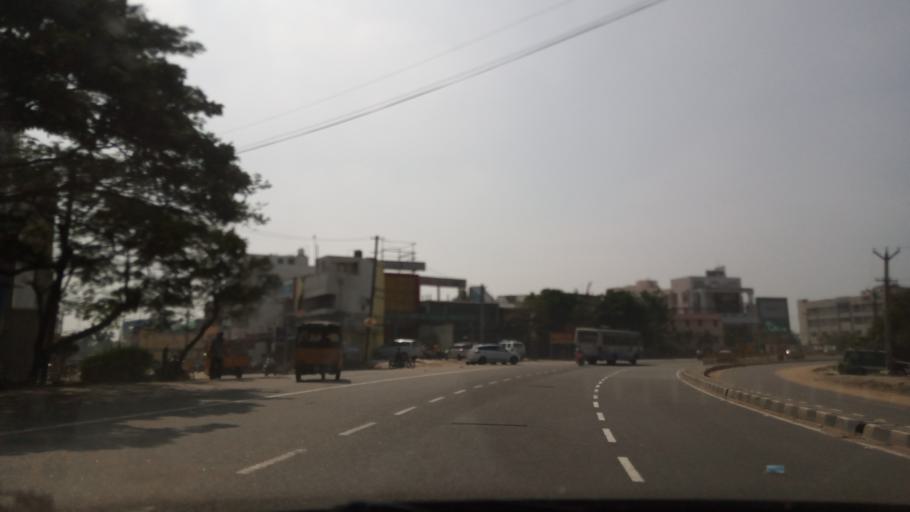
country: IN
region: Tamil Nadu
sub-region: Vellore
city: Arcot
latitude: 12.9114
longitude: 79.3261
